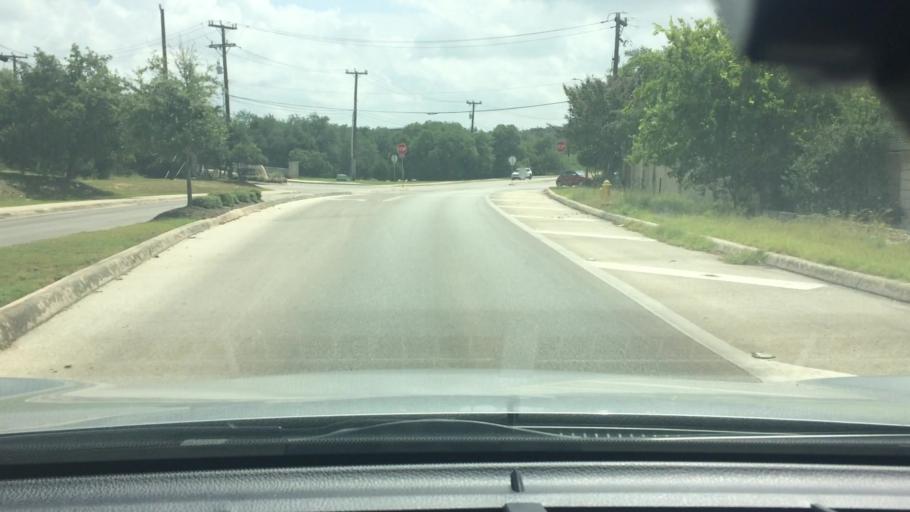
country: US
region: Texas
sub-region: Bexar County
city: Timberwood Park
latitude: 29.6624
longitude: -98.5049
